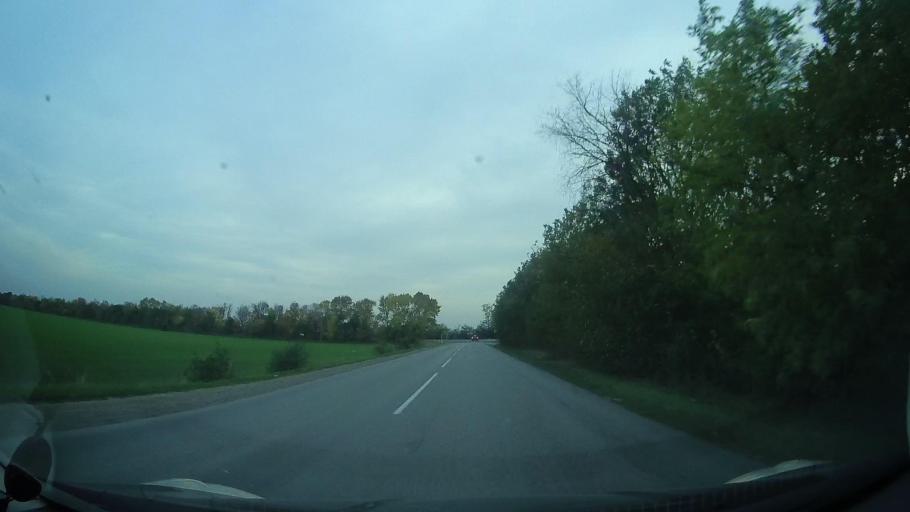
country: RU
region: Rostov
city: Kirovskaya
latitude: 47.0031
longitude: 39.9789
